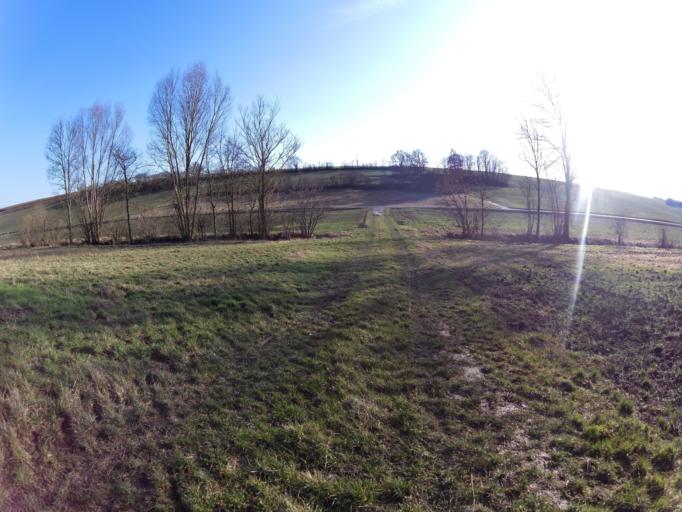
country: DE
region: Bavaria
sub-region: Regierungsbezirk Unterfranken
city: Giebelstadt
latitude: 49.6723
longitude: 9.9822
